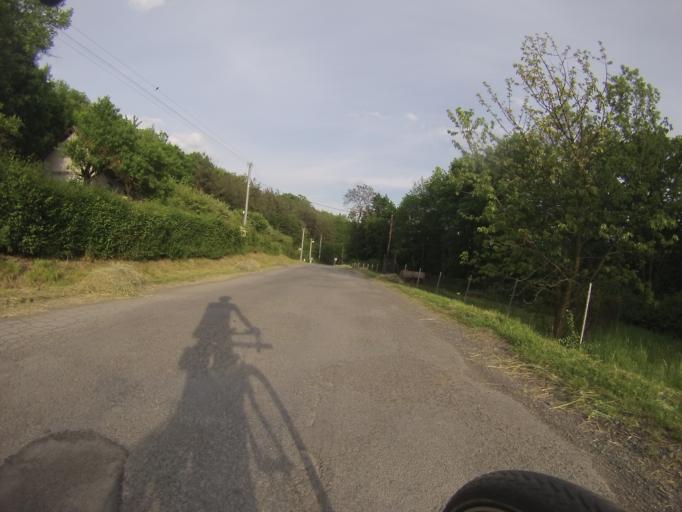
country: CZ
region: Olomoucky
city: Pteni
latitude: 49.4737
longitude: 16.9647
